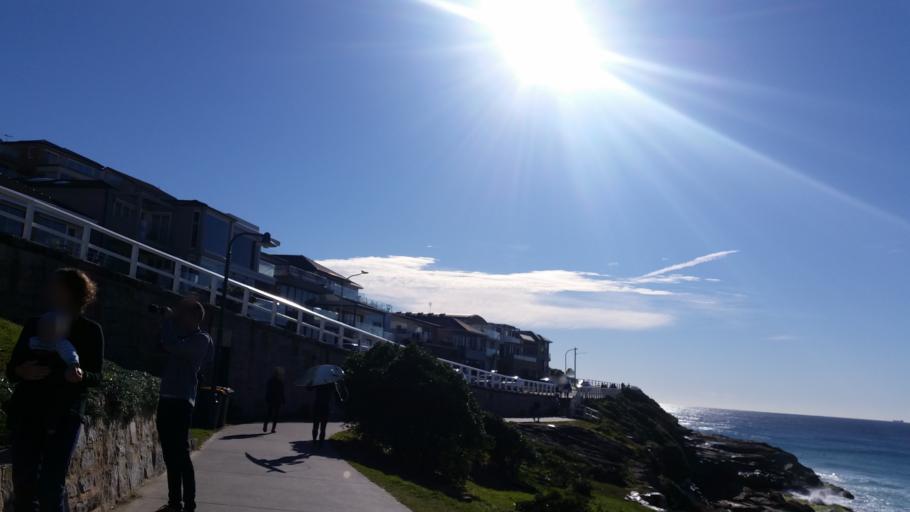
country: AU
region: New South Wales
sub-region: Waverley
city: Bronte
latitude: -33.9027
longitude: 151.2683
